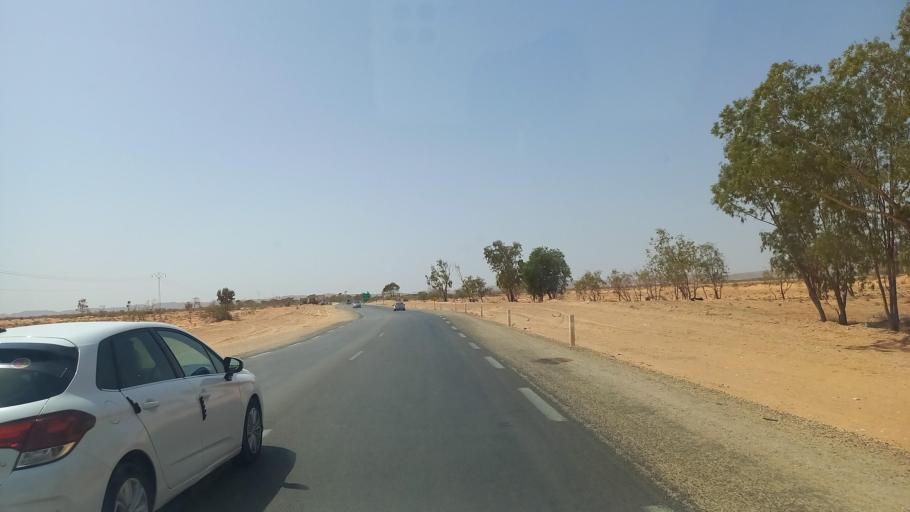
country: TN
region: Madanin
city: Medenine
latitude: 33.2108
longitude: 10.4461
